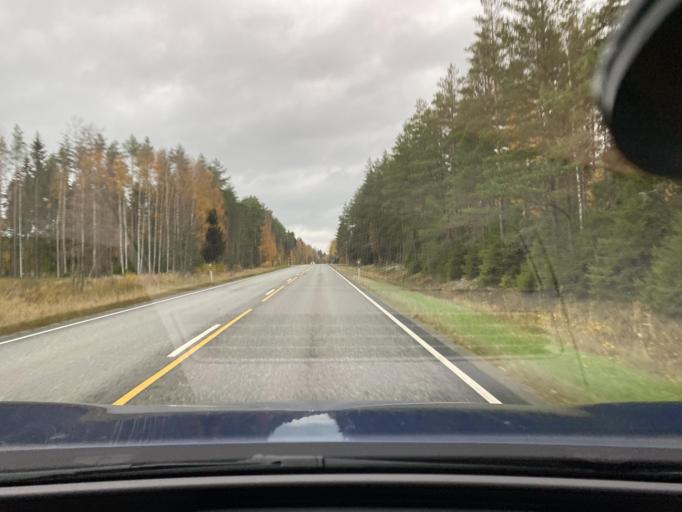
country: FI
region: Varsinais-Suomi
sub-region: Loimaa
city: Ylaene
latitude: 60.8974
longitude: 22.4060
